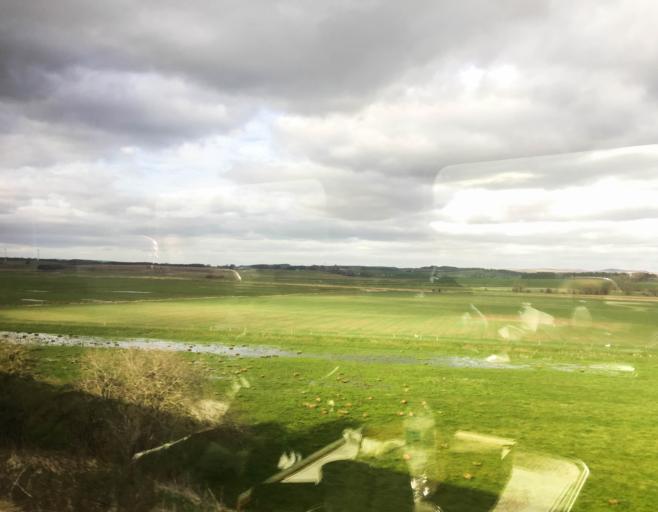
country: GB
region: Scotland
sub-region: South Lanarkshire
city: Carnwath
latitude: 55.6675
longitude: -3.6364
